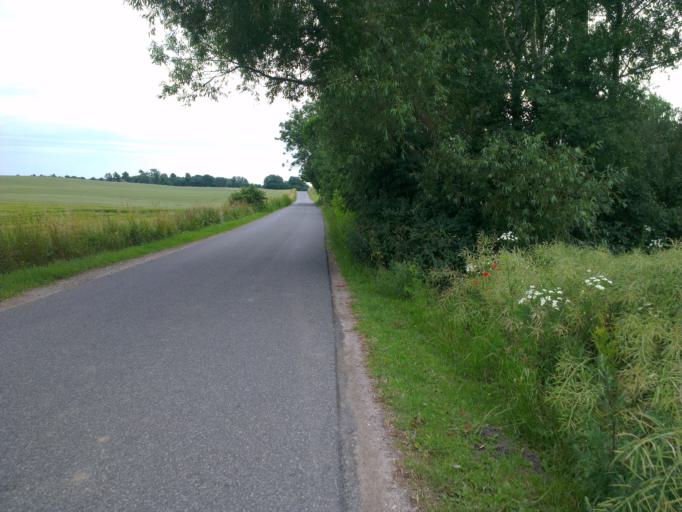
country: DK
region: Capital Region
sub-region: Frederikssund Kommune
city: Skibby
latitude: 55.7504
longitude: 12.0089
